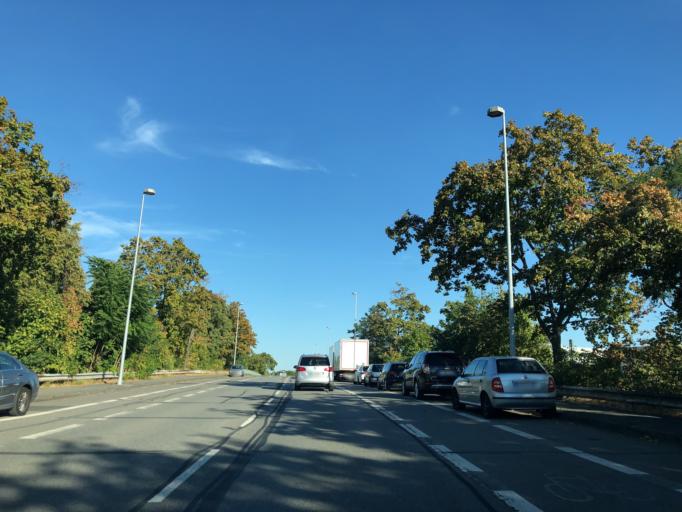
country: DE
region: Rheinland-Pfalz
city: Mainz
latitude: 50.0042
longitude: 8.2918
